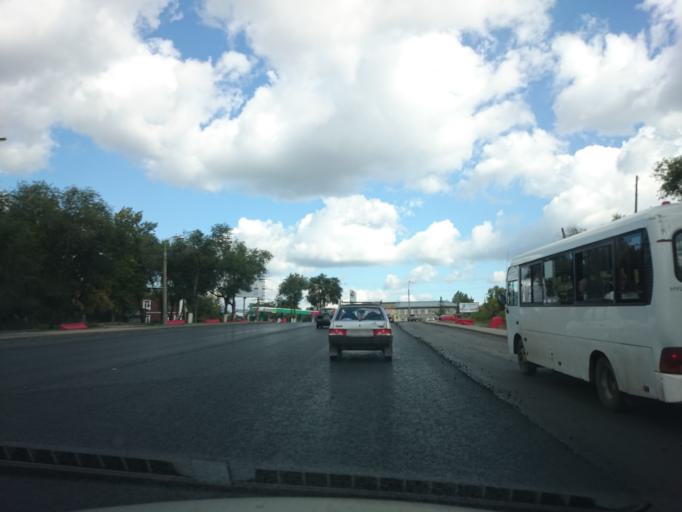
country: RU
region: Samara
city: Samara
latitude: 53.2211
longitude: 50.1650
